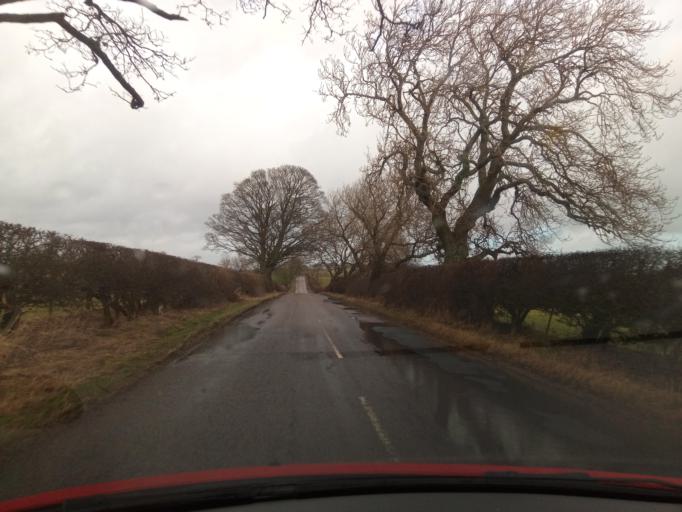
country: GB
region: England
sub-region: Northumberland
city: Rothley
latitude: 55.1828
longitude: -1.9687
